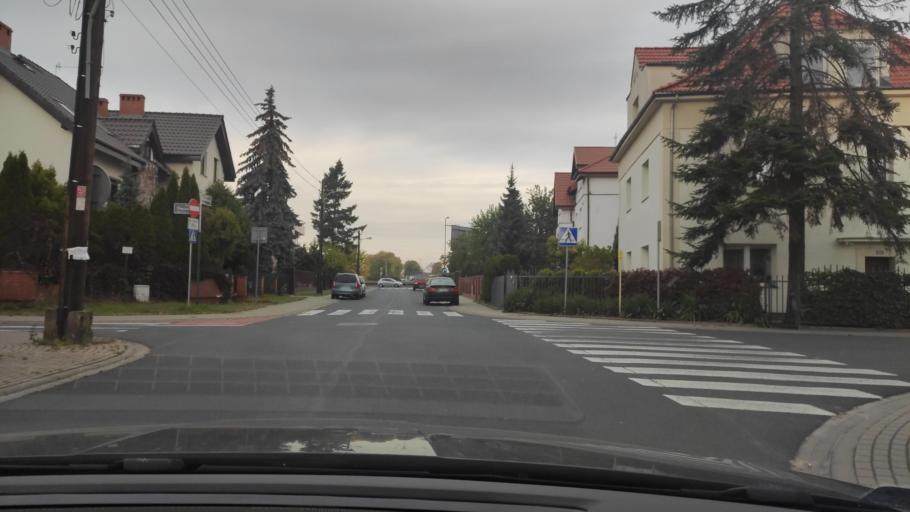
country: PL
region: Greater Poland Voivodeship
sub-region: Powiat poznanski
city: Lubon
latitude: 52.3754
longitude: 16.8733
